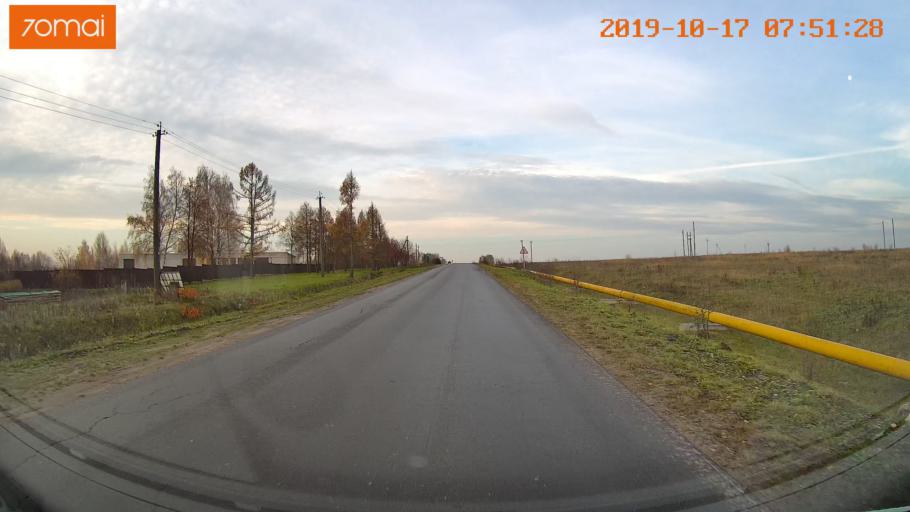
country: RU
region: Vladimir
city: Yur'yev-Pol'skiy
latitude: 56.4812
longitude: 39.6552
